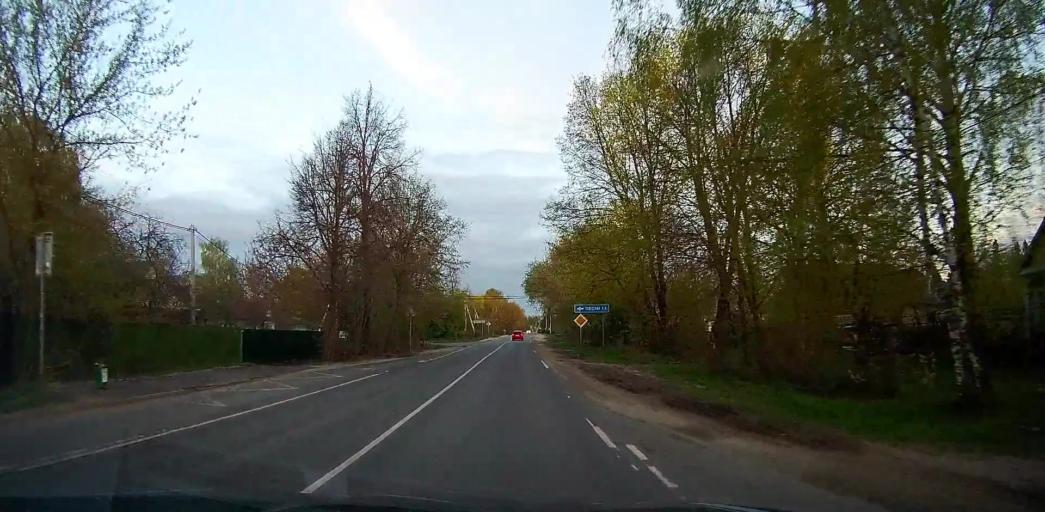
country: RU
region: Moskovskaya
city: Peski
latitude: 55.2072
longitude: 38.7394
